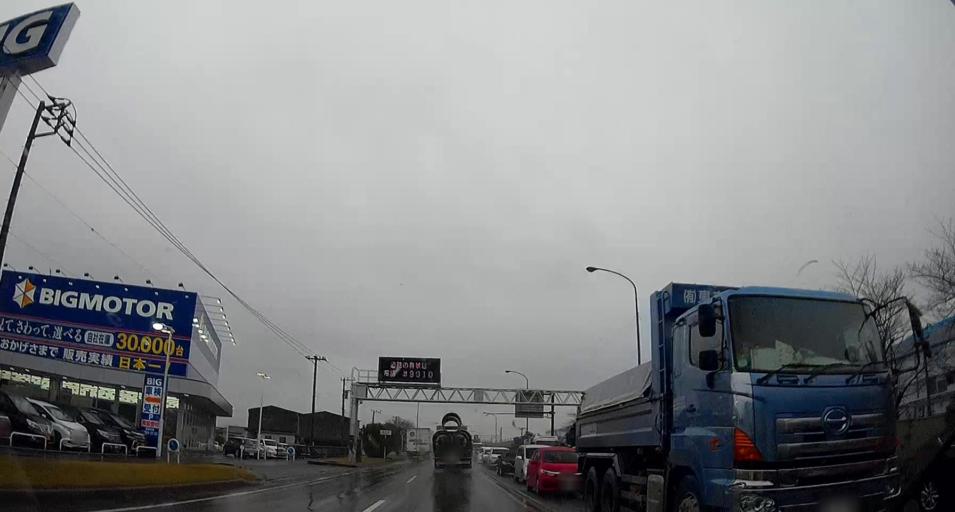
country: JP
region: Chiba
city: Chiba
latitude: 35.5606
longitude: 140.1275
